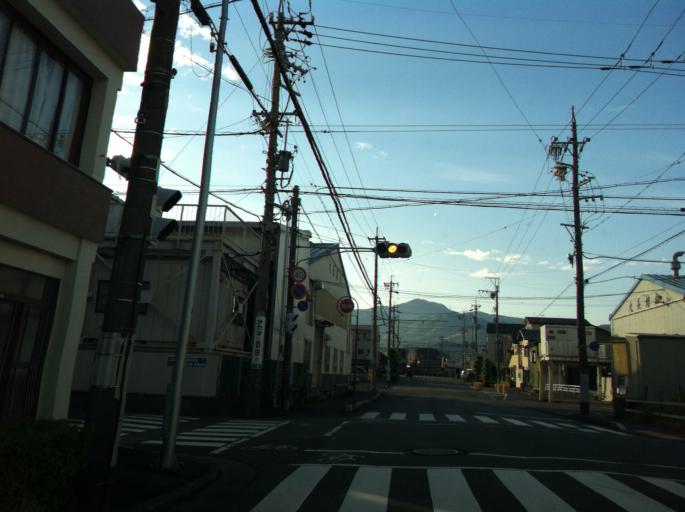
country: JP
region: Shizuoka
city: Shizuoka-shi
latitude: 35.0207
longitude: 138.4732
